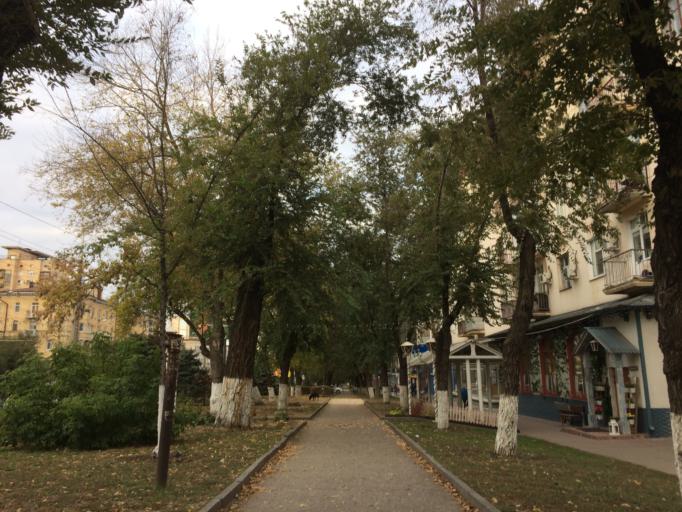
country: RU
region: Volgograd
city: Volgograd
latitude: 48.7197
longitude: 44.5326
